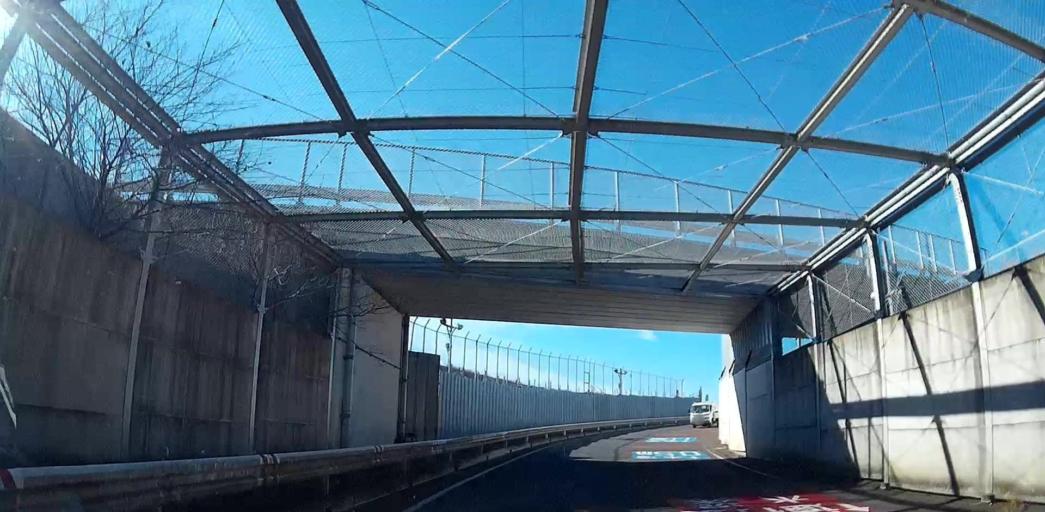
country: JP
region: Chiba
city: Narita
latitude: 35.7844
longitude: 140.3959
